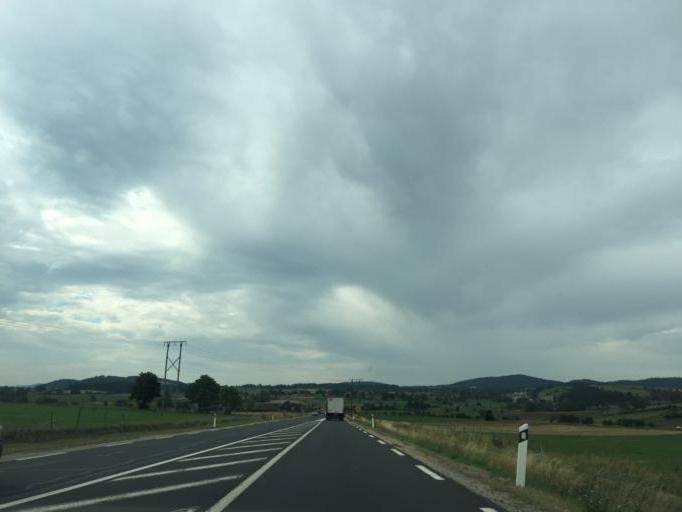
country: FR
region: Auvergne
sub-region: Departement de la Haute-Loire
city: Solignac-sur-Loire
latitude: 44.9304
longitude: 3.8442
